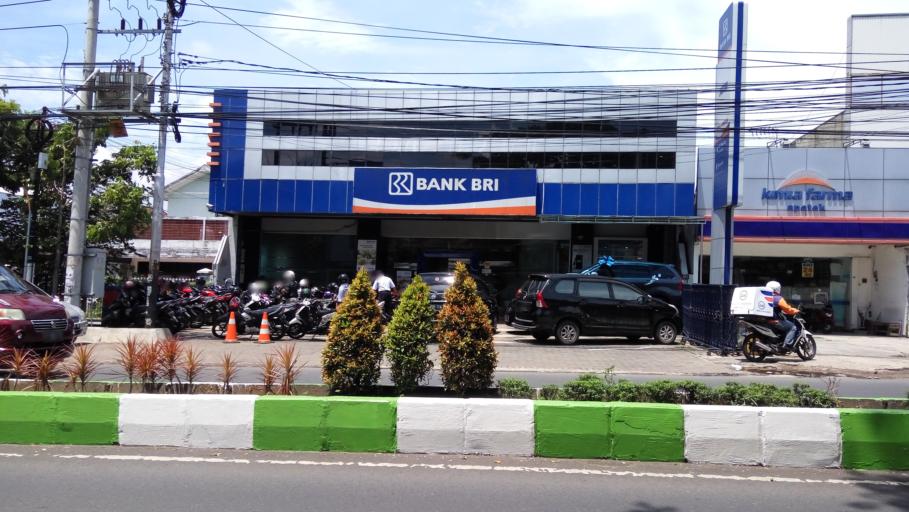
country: ID
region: East Java
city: Malang
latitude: -7.9558
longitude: 112.6384
